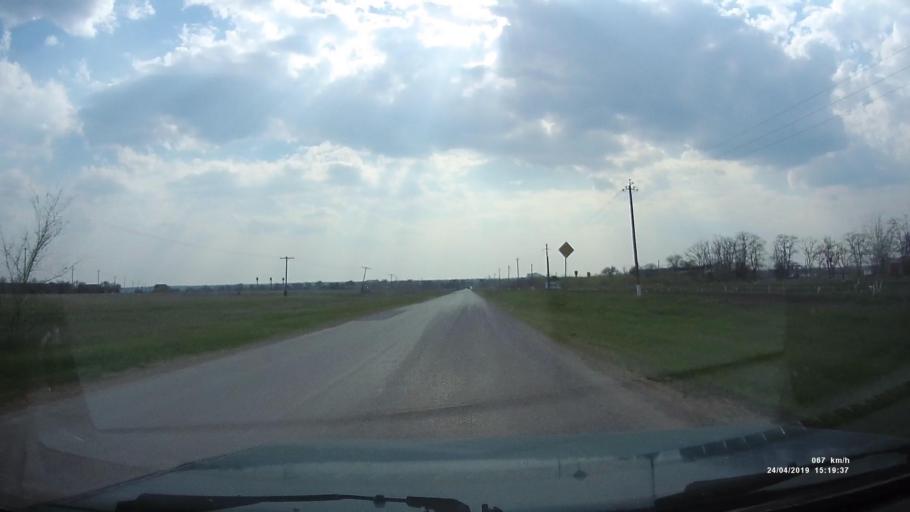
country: RU
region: Rostov
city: Remontnoye
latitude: 46.5390
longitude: 43.1434
